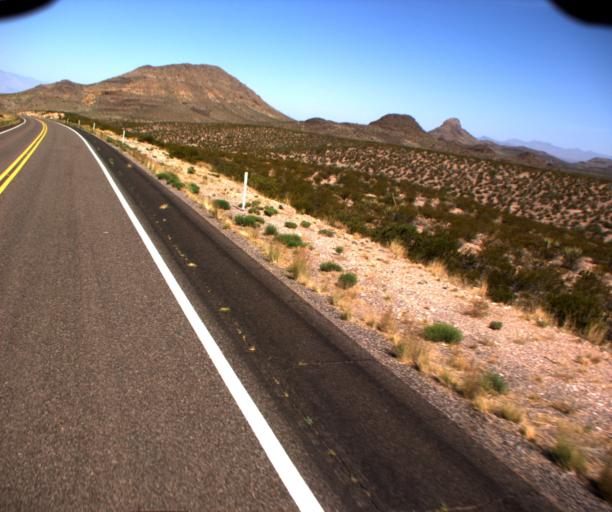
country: US
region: Arizona
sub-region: Greenlee County
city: Clifton
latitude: 32.7542
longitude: -109.3643
